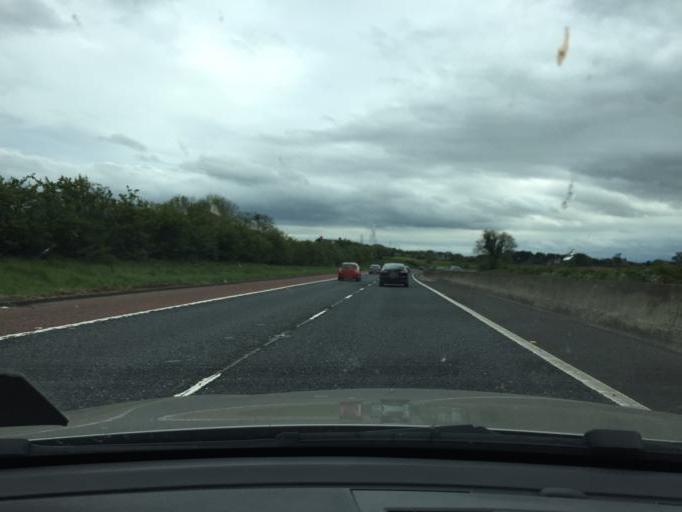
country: GB
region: Northern Ireland
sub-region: Lisburn District
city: Lisburn
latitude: 54.5183
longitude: -6.0081
